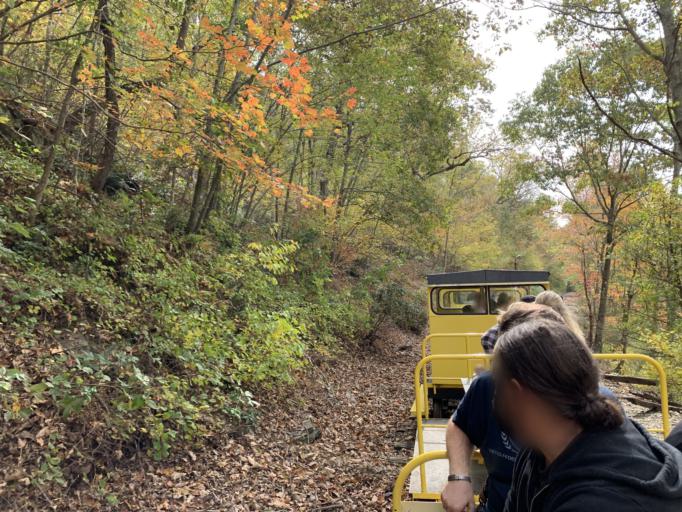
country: US
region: Pennsylvania
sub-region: York County
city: Susquehanna Trails
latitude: 39.8121
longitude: -76.4760
